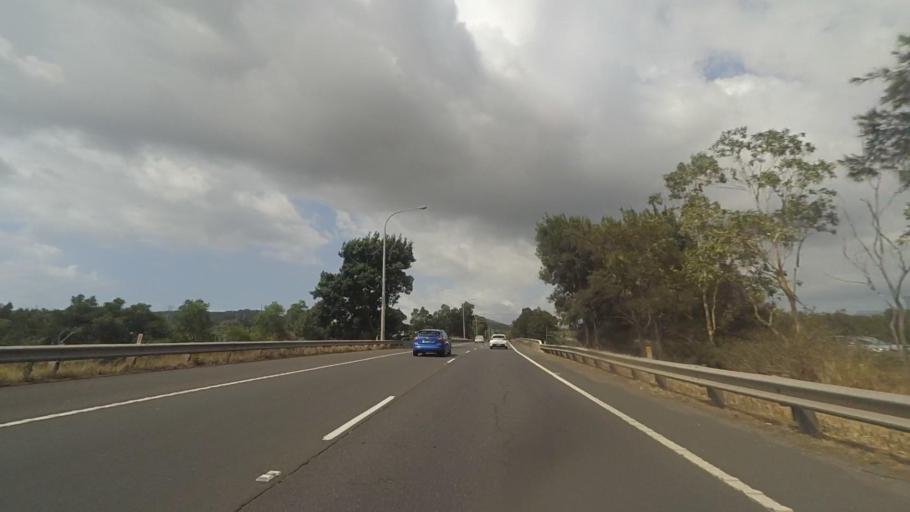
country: AU
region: New South Wales
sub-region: Wollongong
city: Mount Saint Thomas
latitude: -34.4542
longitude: 150.8583
